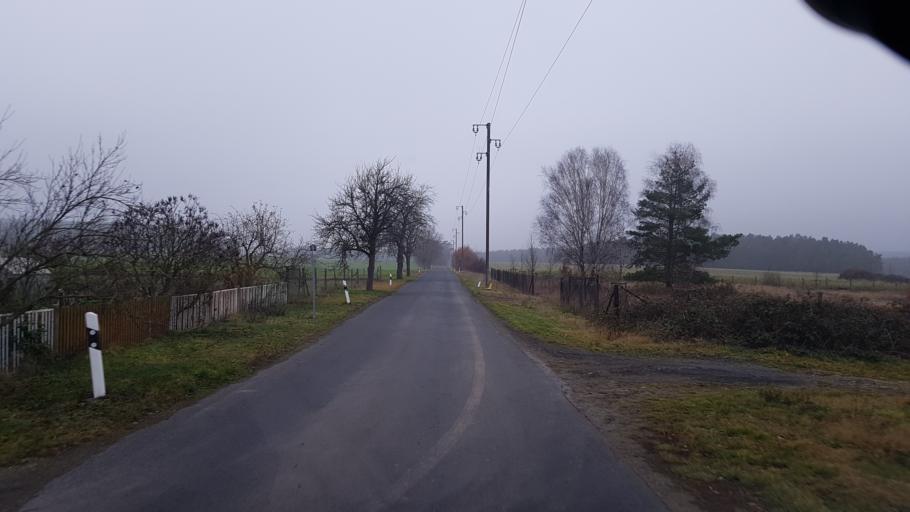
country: DE
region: Brandenburg
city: Altdobern
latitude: 51.6776
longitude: 13.9851
